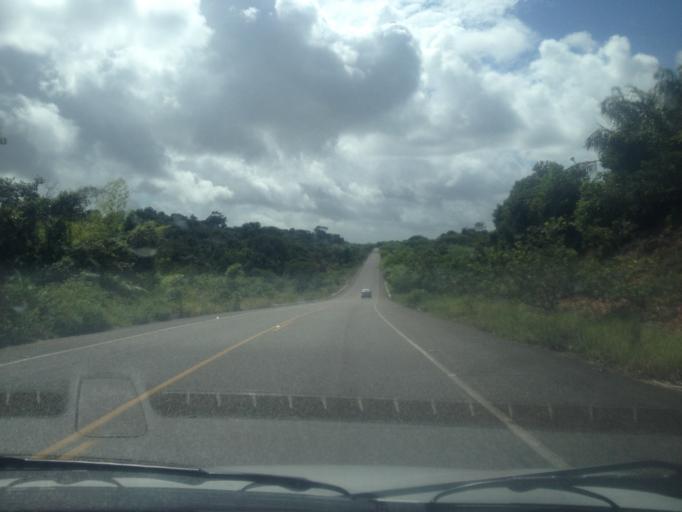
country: BR
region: Bahia
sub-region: Entre Rios
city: Entre Rios
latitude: -12.1922
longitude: -37.8219
